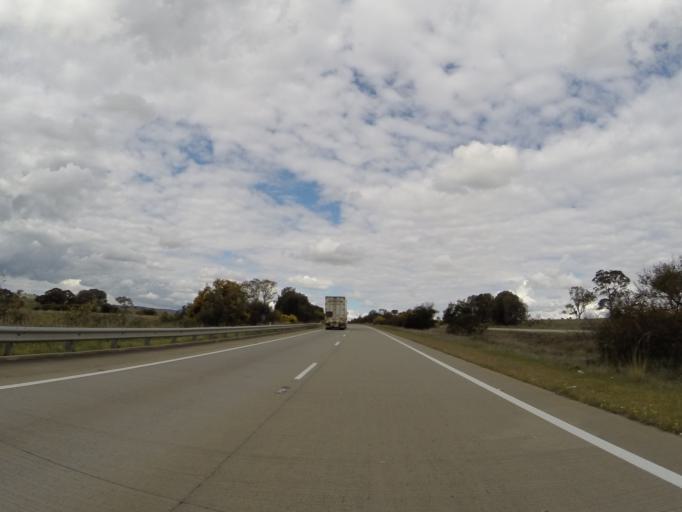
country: AU
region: New South Wales
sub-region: Yass Valley
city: Gundaroo
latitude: -34.8117
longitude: 149.3182
